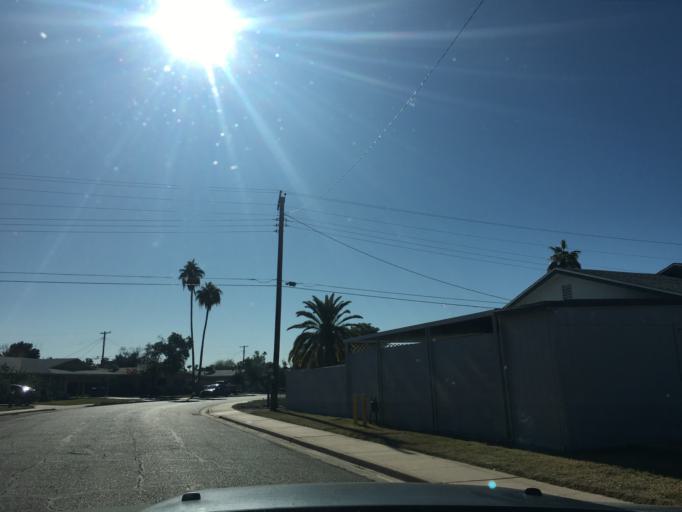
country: US
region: Arizona
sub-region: Maricopa County
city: Mesa
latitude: 33.4473
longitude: -111.8498
